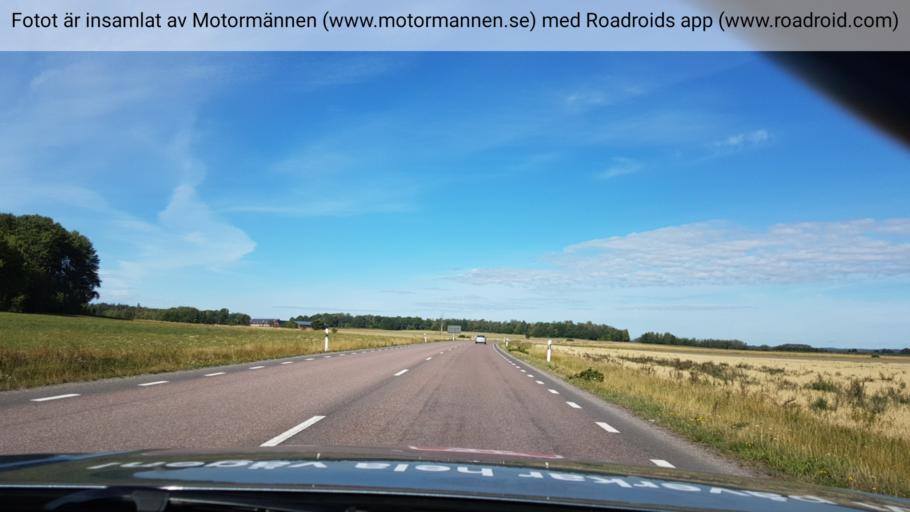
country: SE
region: Uppsala
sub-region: Uppsala Kommun
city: Gamla Uppsala
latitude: 59.8794
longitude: 17.5779
